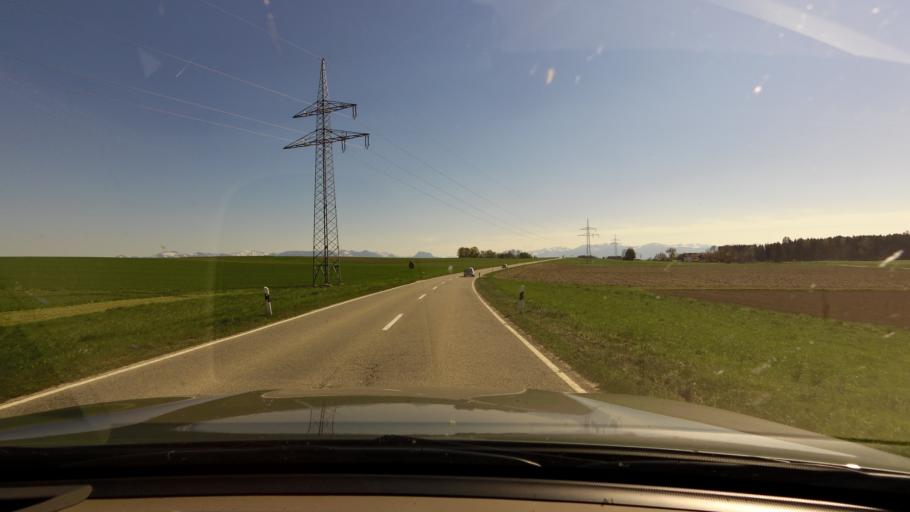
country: DE
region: Bavaria
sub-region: Upper Bavaria
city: Griesstatt
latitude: 47.9775
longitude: 12.1772
